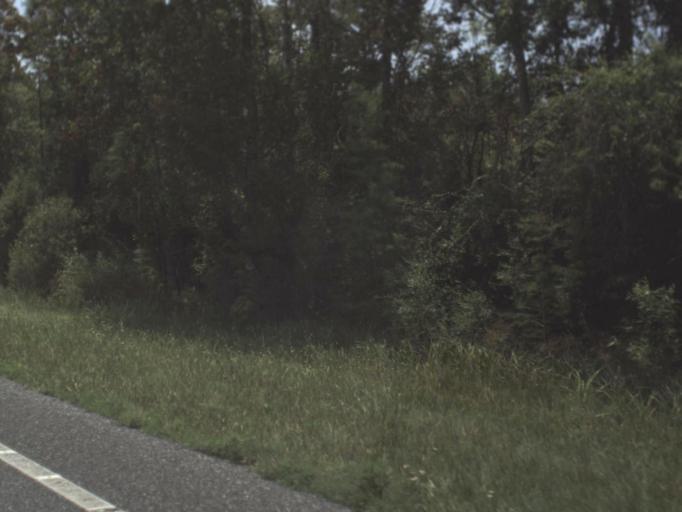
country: US
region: Florida
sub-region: Taylor County
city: Steinhatchee
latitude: 29.8730
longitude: -83.4010
